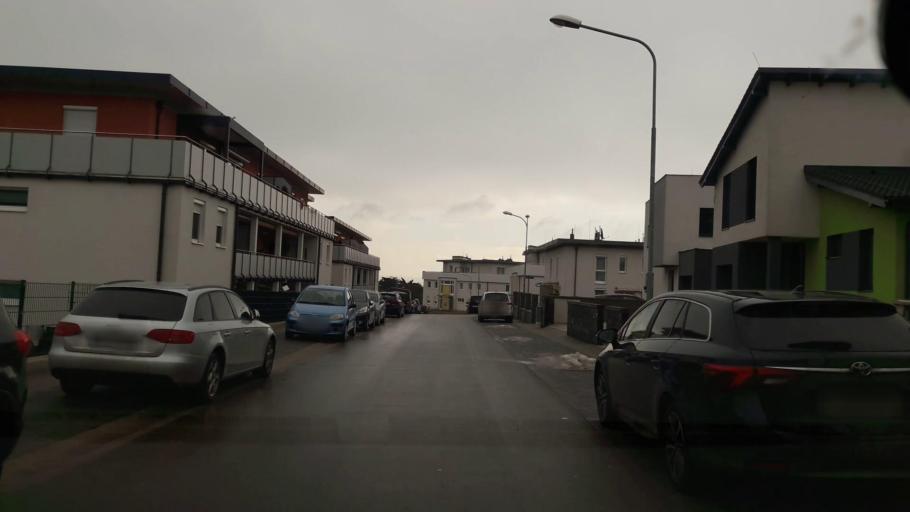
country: AT
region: Lower Austria
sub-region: Politischer Bezirk Bruck an der Leitha
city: Hainburg an der Donau
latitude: 48.1394
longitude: 16.9559
